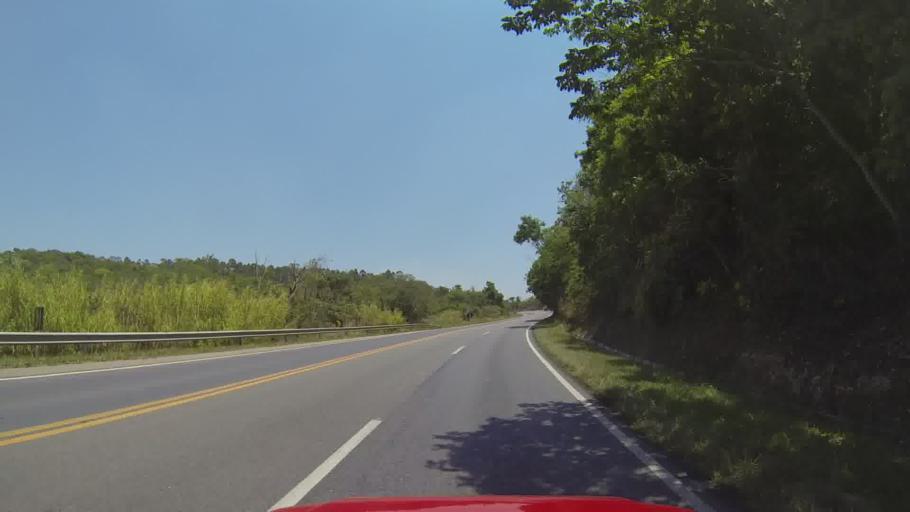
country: BR
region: Minas Gerais
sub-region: Itapecerica
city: Itapecerica
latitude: -20.2983
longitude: -45.1933
